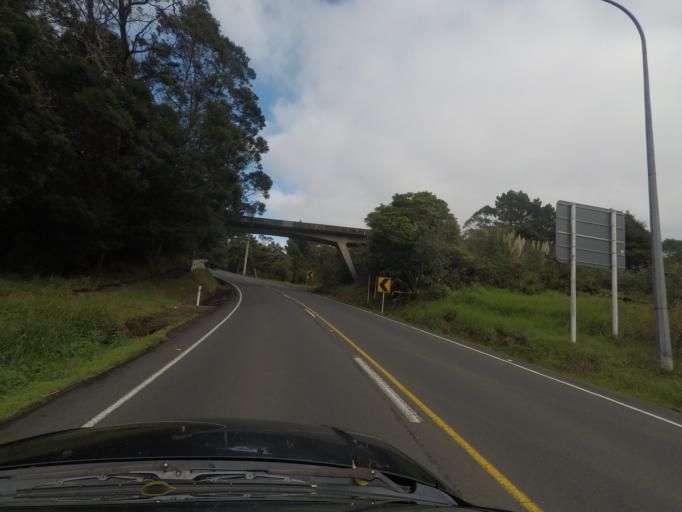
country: NZ
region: Auckland
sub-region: Auckland
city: Rosebank
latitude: -36.8653
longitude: 174.5651
